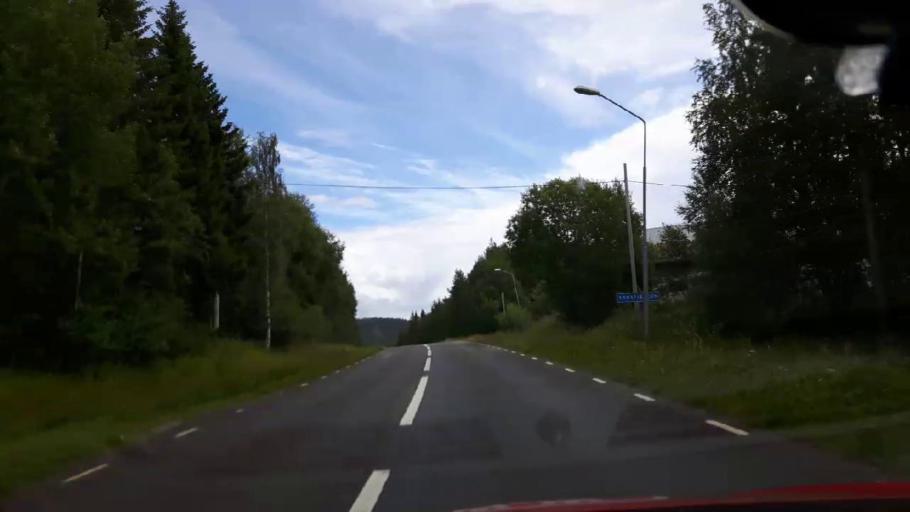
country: SE
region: Jaemtland
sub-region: Stroemsunds Kommun
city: Stroemsund
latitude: 64.3364
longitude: 14.9613
